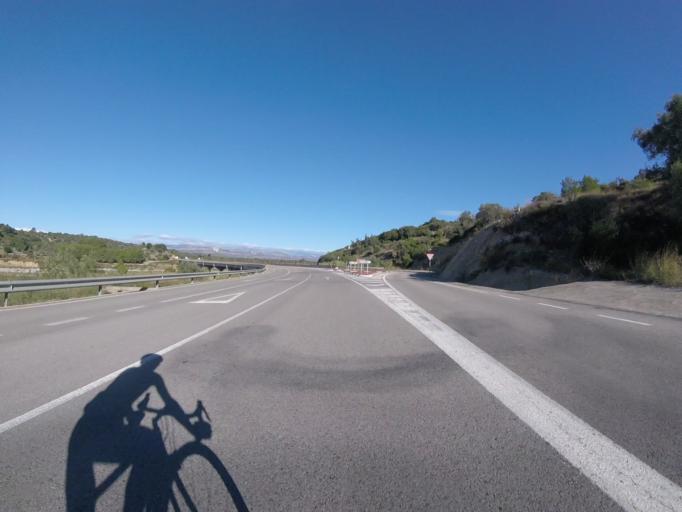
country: ES
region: Valencia
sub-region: Provincia de Castello
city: Cervera del Maestre
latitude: 40.4648
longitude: 0.2512
